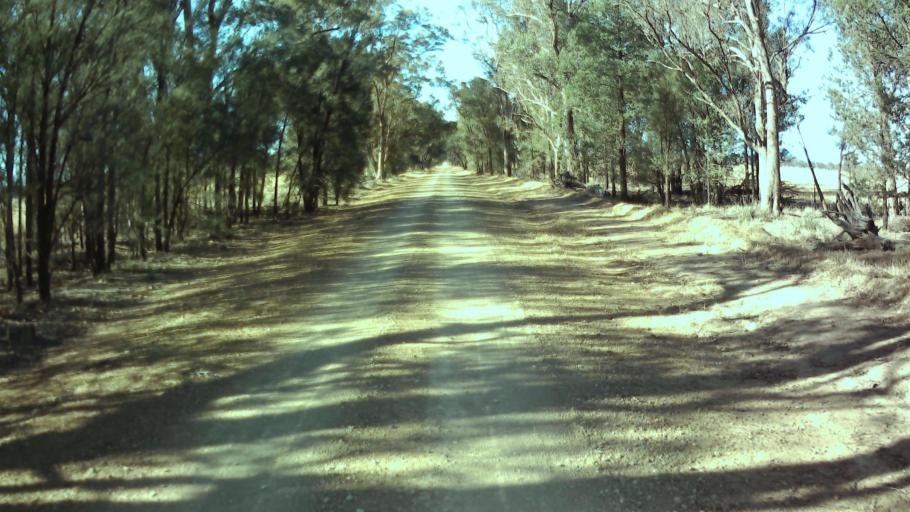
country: AU
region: New South Wales
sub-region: Weddin
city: Grenfell
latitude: -33.8188
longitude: 147.8758
